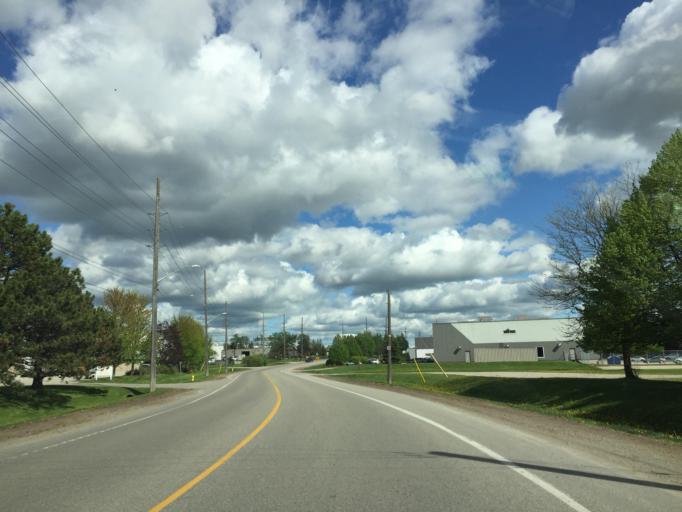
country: CA
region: Ontario
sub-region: Wellington County
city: Guelph
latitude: 43.4907
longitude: -80.2066
